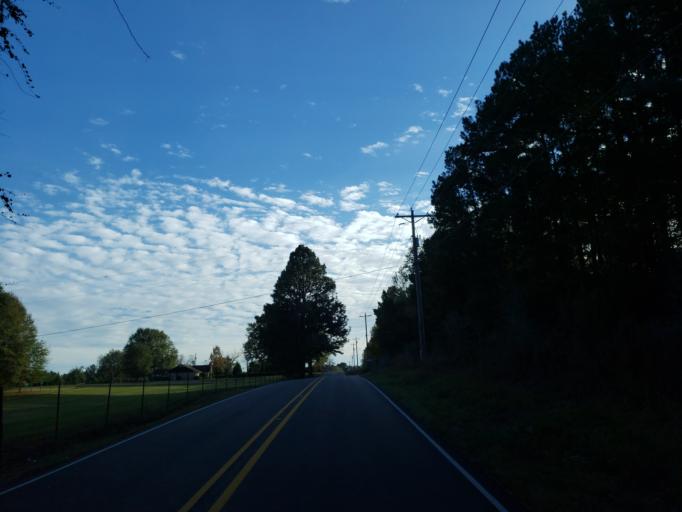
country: US
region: Mississippi
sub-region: Lamar County
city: West Hattiesburg
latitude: 31.2975
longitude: -89.3988
